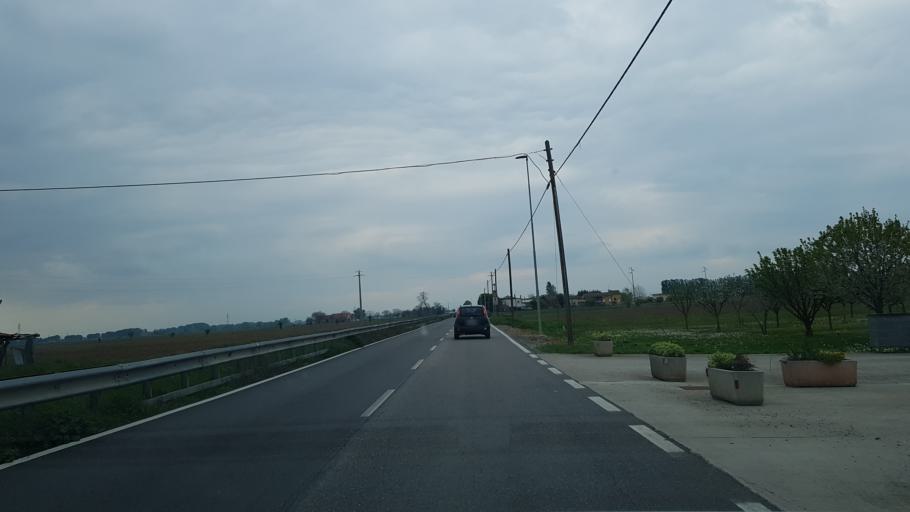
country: IT
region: Veneto
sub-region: Provincia di Verona
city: Casaleone
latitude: 45.1506
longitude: 11.2298
